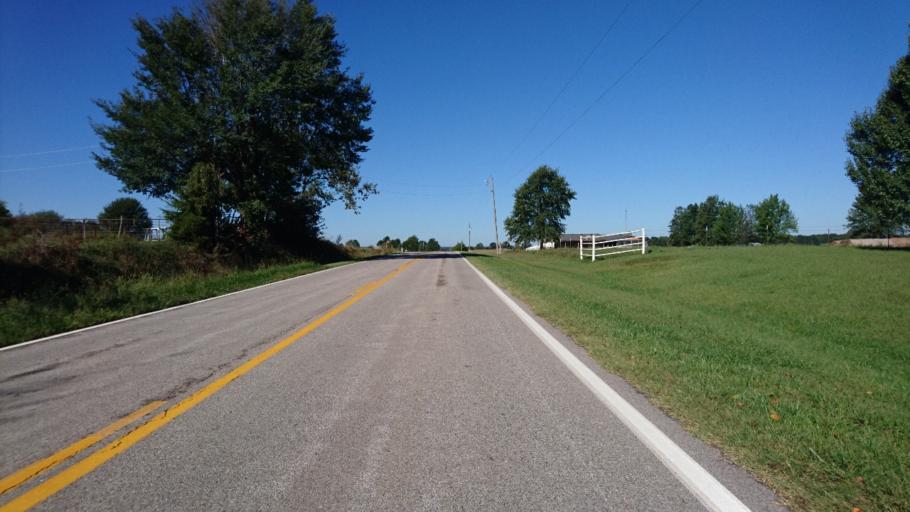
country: US
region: Missouri
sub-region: Greene County
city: Ash Grove
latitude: 37.1939
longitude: -93.6557
